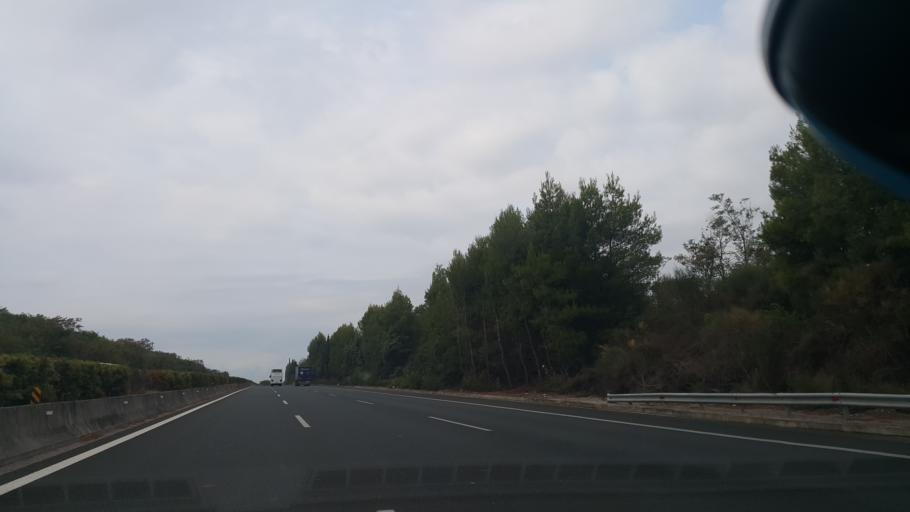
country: GR
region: Central Macedonia
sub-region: Nomos Pierias
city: Kitros
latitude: 40.3520
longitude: 22.5965
